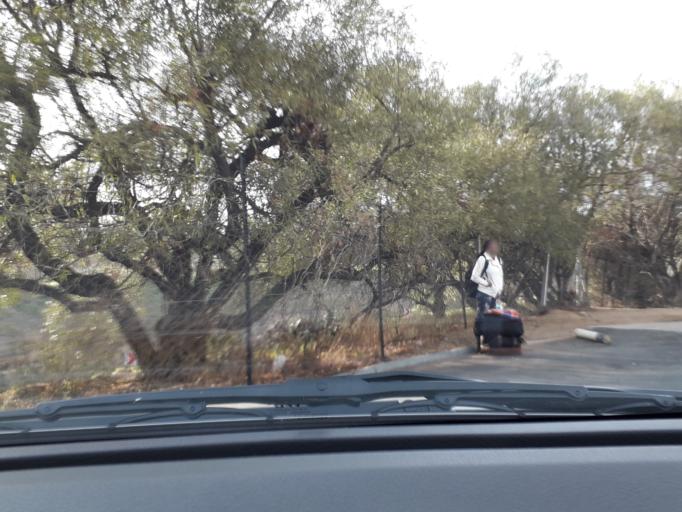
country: ZA
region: Gauteng
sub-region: City of Johannesburg Metropolitan Municipality
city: Midrand
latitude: -25.9300
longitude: 28.1461
